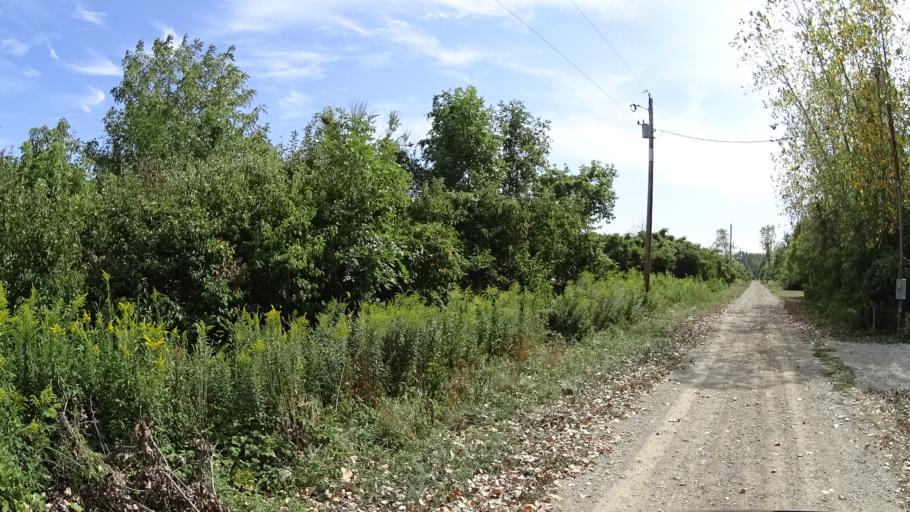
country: US
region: Ohio
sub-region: Erie County
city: Sandusky
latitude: 41.5909
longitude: -82.6933
